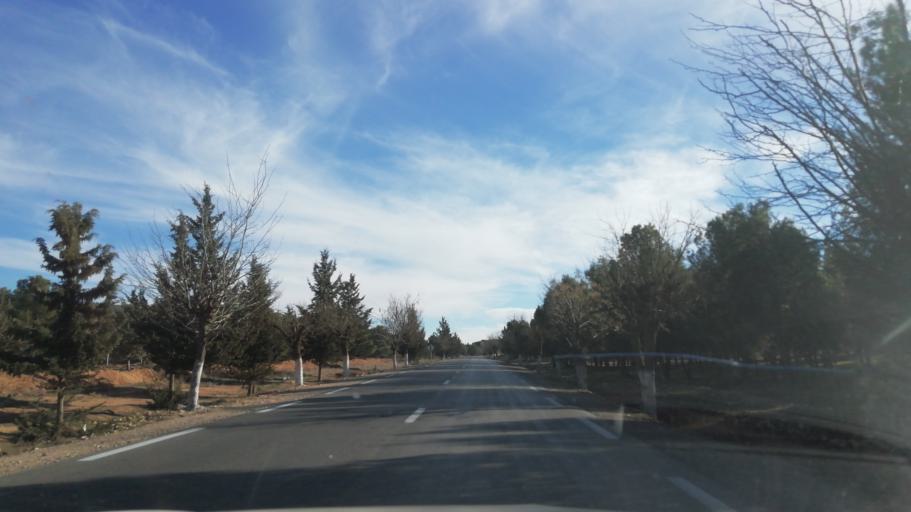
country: DZ
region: Tlemcen
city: Sebdou
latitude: 34.6162
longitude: -1.3335
